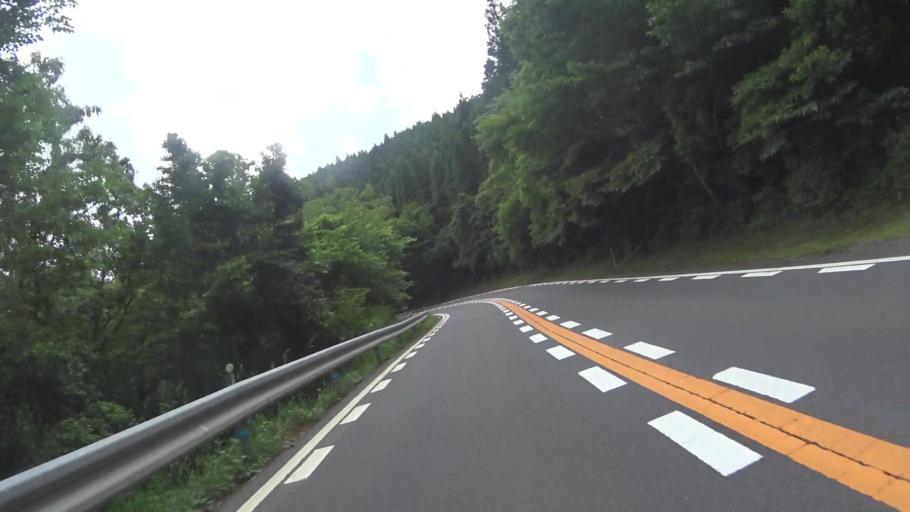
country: JP
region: Oita
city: Tsukawaki
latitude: 33.2300
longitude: 131.2958
